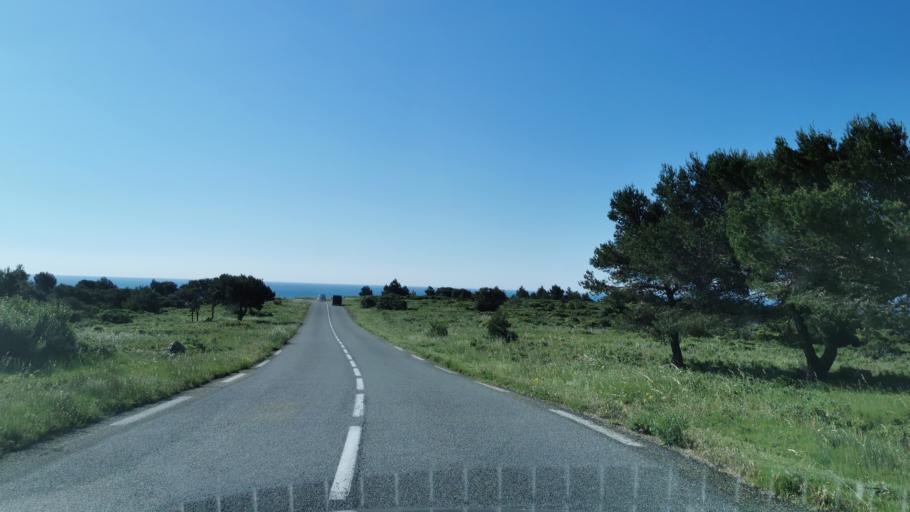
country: FR
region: Languedoc-Roussillon
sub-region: Departement de l'Aude
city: Armissan
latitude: 43.1630
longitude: 3.1346
